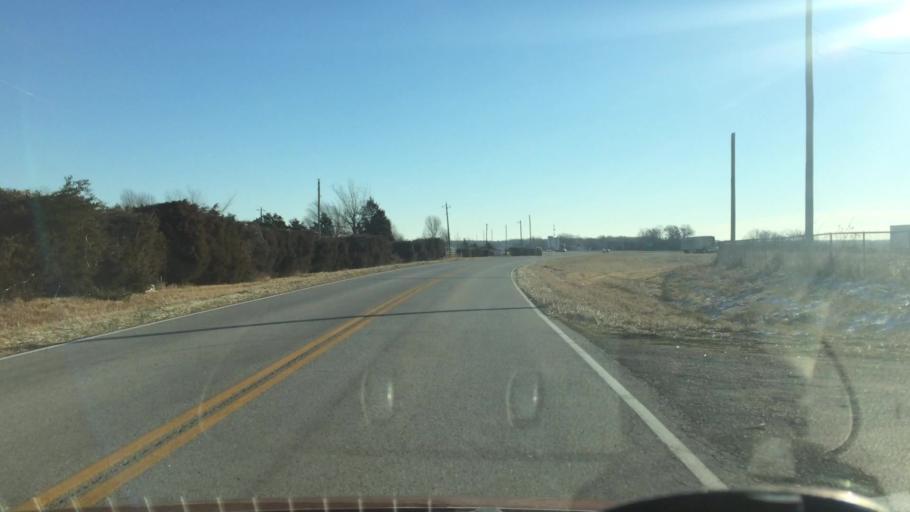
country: US
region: Missouri
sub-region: Greene County
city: Strafford
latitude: 37.2715
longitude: -93.1012
